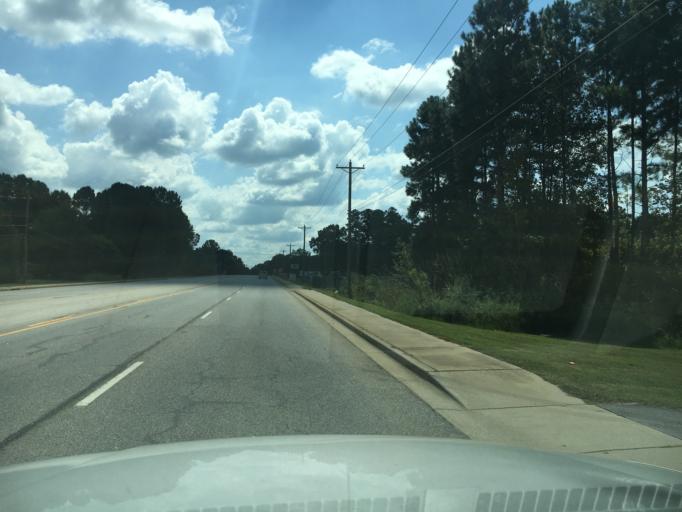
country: US
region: South Carolina
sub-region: Greenwood County
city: Greenwood
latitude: 34.1851
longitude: -82.1834
